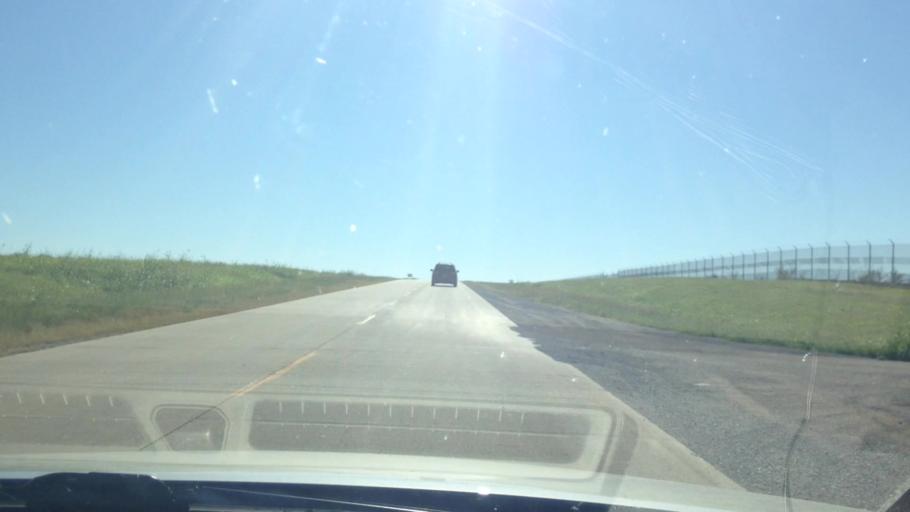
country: US
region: Missouri
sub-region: Platte County
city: Platte City
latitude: 39.3318
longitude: -94.7195
